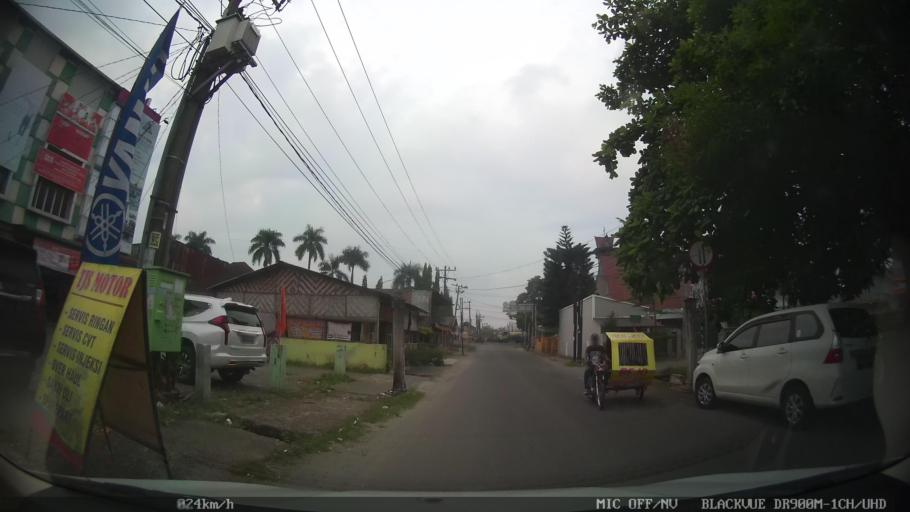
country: ID
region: North Sumatra
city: Deli Tua
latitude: 3.5396
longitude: 98.6983
